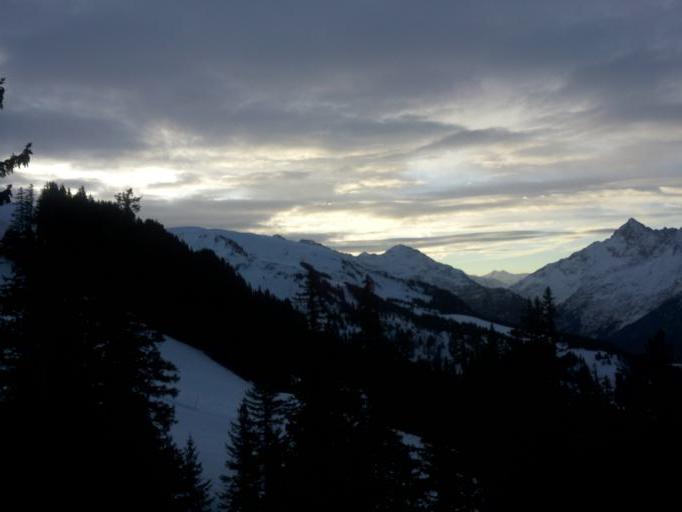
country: CH
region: Bern
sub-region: Interlaken-Oberhasli District
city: Meiringen
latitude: 46.7564
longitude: 8.2167
